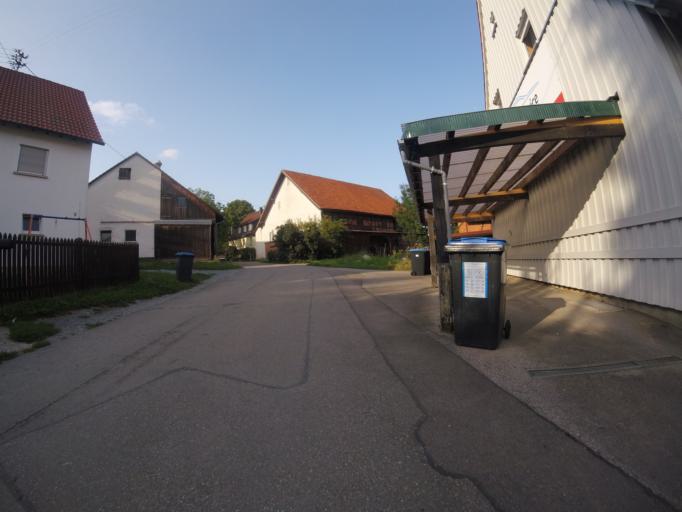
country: DE
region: Baden-Wuerttemberg
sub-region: Regierungsbezirk Stuttgart
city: Backnang
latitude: 48.9705
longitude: 9.4362
